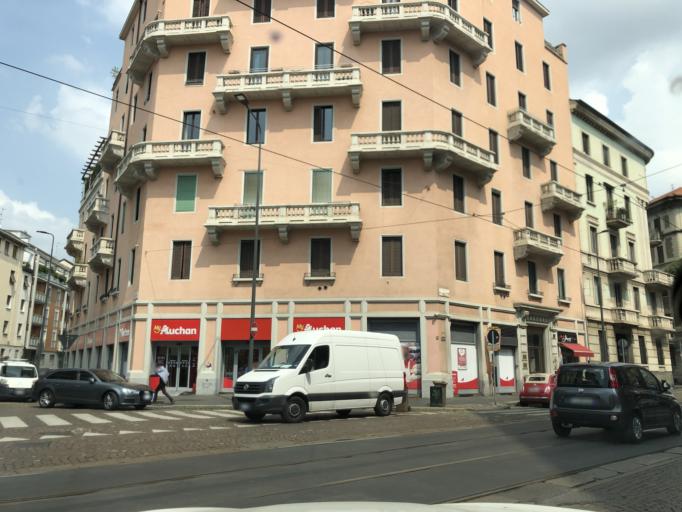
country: IT
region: Lombardy
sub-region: Citta metropolitana di Milano
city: Milano
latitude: 45.4895
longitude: 9.2143
